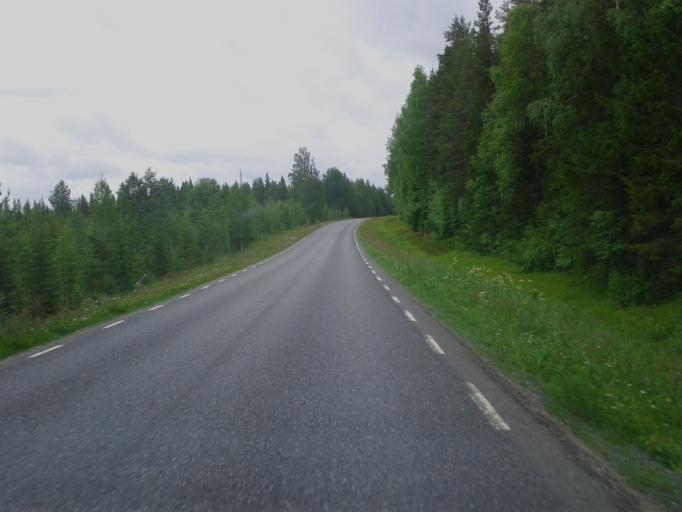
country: SE
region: Vaesterbotten
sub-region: Skelleftea Kommun
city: Forsbacka
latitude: 64.8618
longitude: 20.5416
